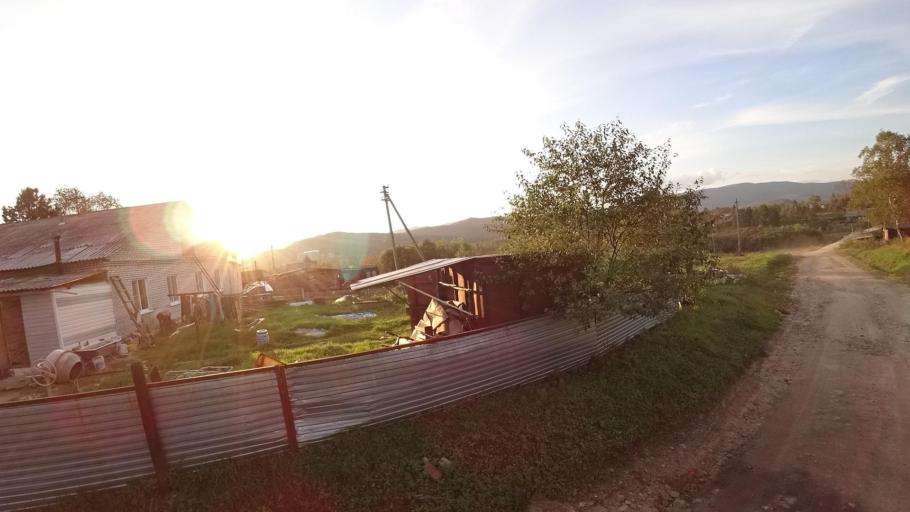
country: RU
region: Jewish Autonomous Oblast
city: Kul'dur
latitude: 49.2043
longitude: 131.6400
